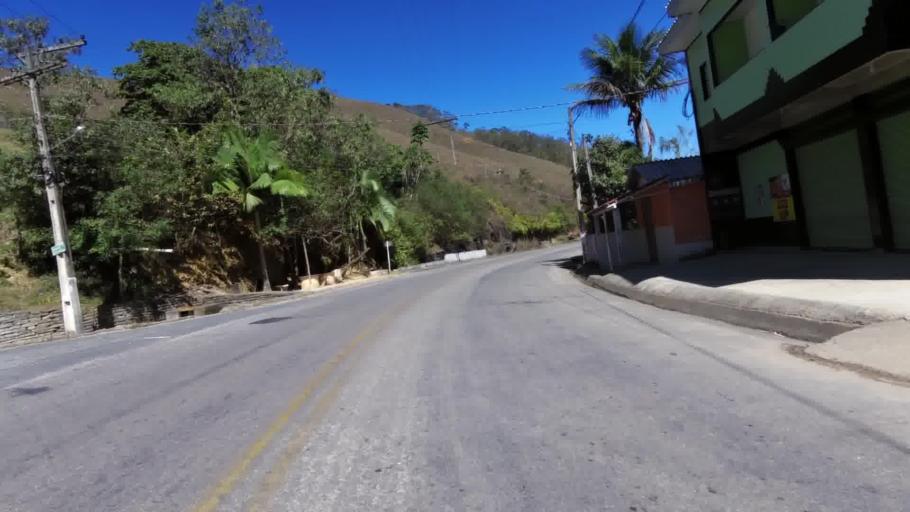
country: BR
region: Espirito Santo
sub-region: Vargem Alta
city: Vargem Alta
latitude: -20.6658
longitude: -40.9902
